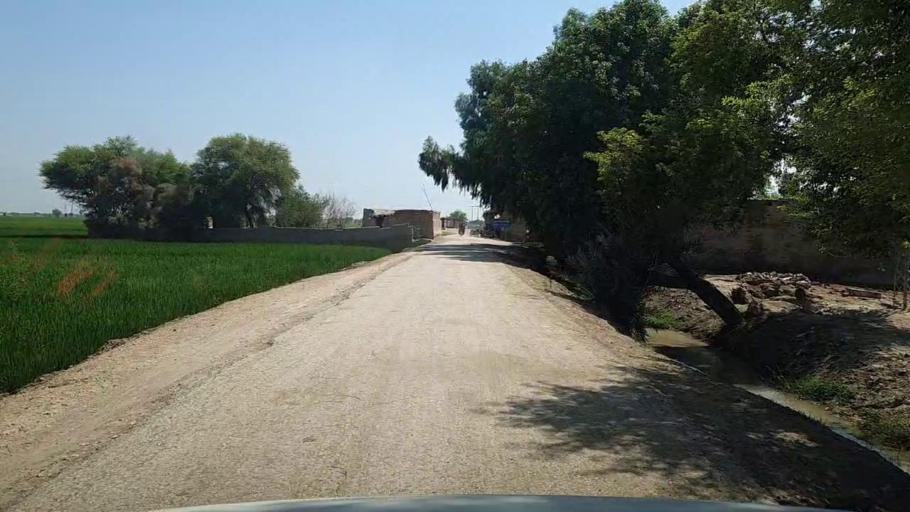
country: PK
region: Sindh
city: Kandhkot
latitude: 28.3197
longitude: 69.3399
